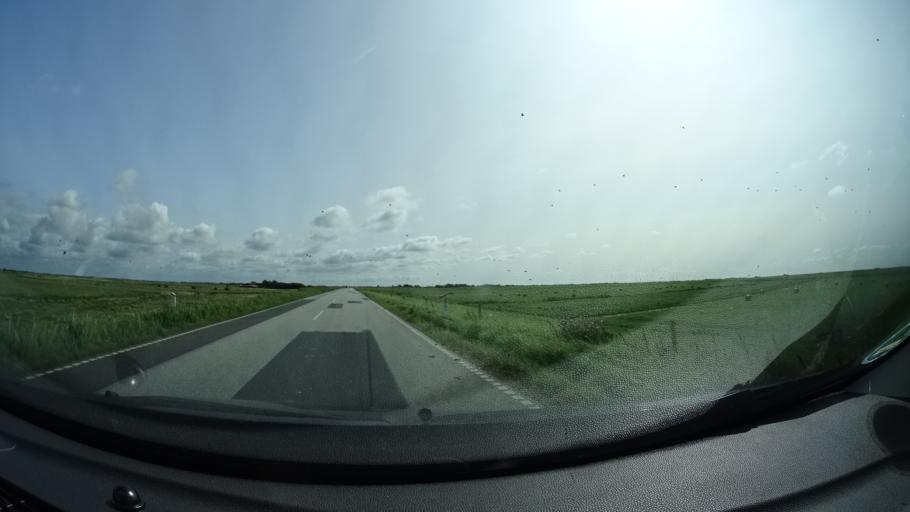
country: DE
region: Schleswig-Holstein
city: Rodenas
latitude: 54.9421
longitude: 8.7101
